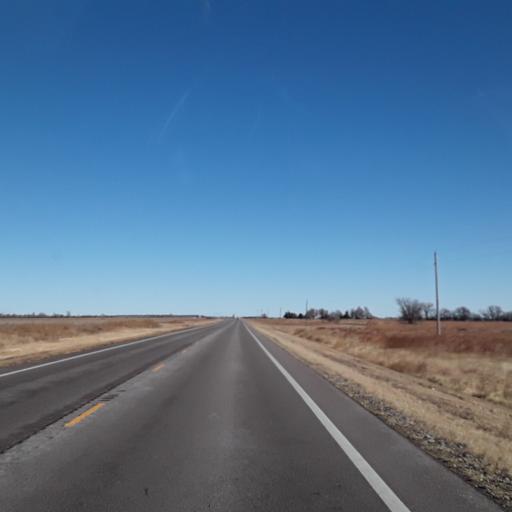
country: US
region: Kansas
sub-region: Pawnee County
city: Larned
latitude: 38.1261
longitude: -99.1703
